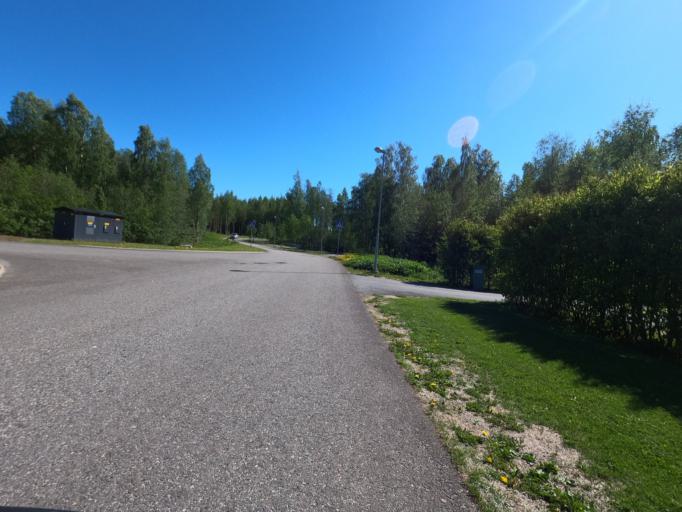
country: FI
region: North Karelia
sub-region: Joensuu
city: Joensuu
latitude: 62.6032
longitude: 29.8250
